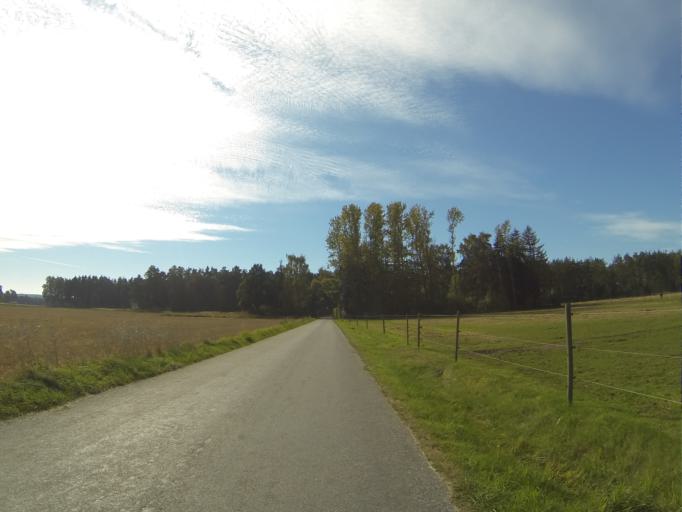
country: SE
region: Skane
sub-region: Eslovs Kommun
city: Eslov
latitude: 55.7350
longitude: 13.3690
